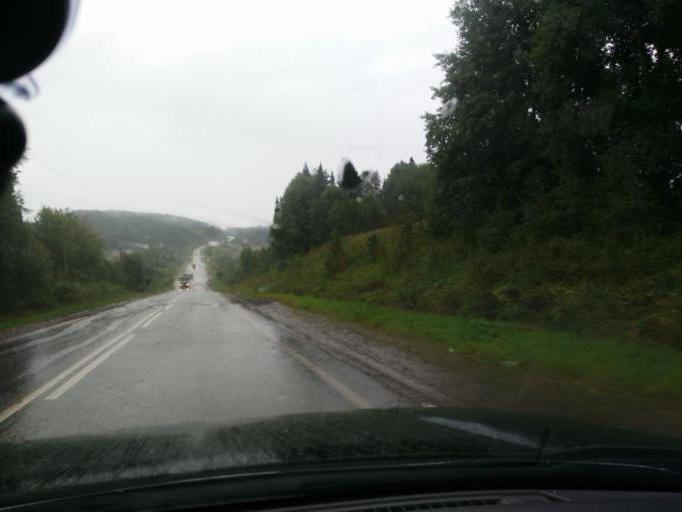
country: RU
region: Perm
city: Osa
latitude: 57.2957
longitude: 55.6122
